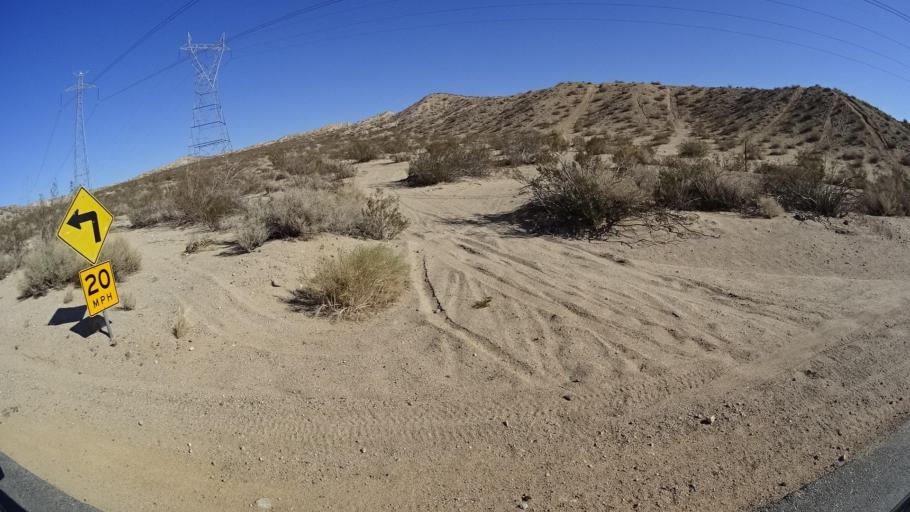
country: US
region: California
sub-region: Kern County
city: California City
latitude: 35.3060
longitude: -118.0097
